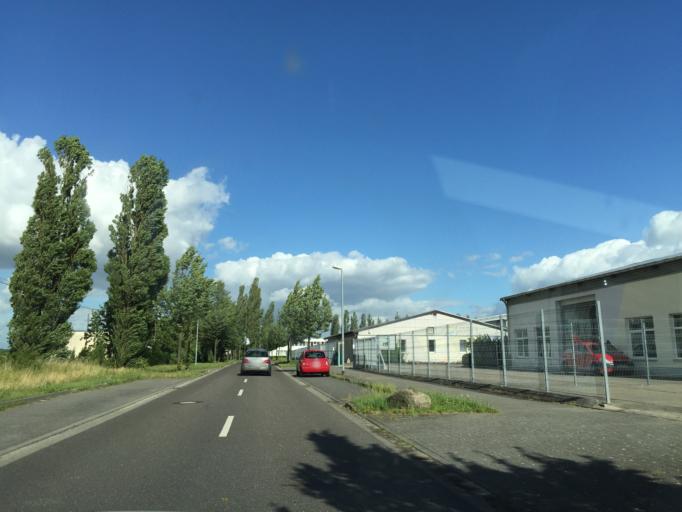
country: DE
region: Mecklenburg-Vorpommern
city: Neubrandenburg
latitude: 53.5233
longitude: 13.2691
